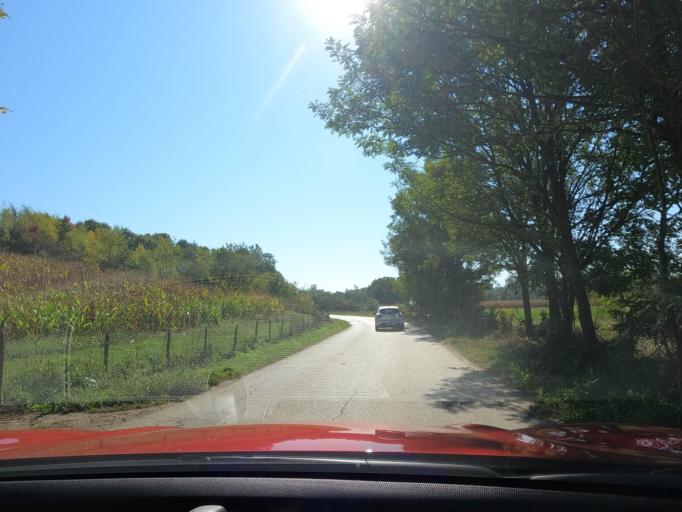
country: RS
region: Central Serbia
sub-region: Raski Okrug
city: Kraljevo
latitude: 43.7772
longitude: 20.6519
